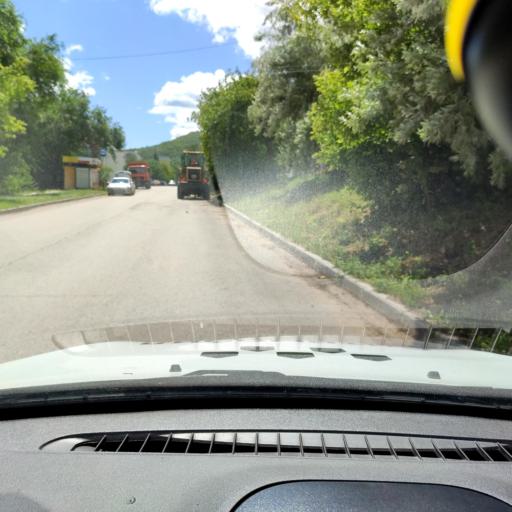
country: RU
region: Samara
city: Zhigulevsk
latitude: 53.4084
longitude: 49.4067
